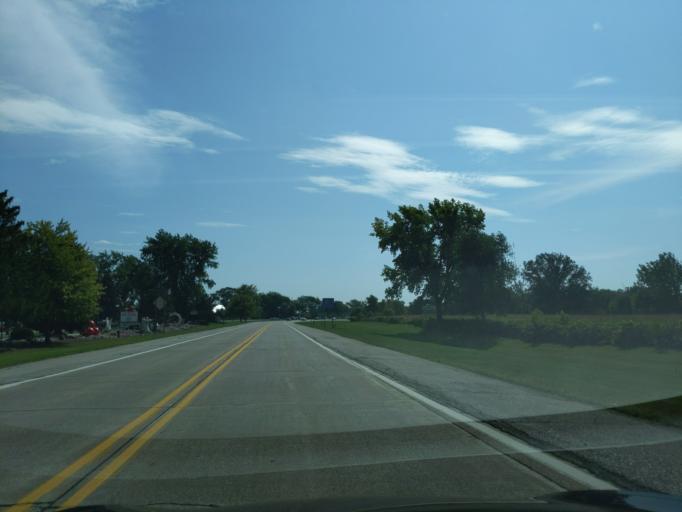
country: US
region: Michigan
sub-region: Saginaw County
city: Frankenmuth
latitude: 43.3131
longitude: -83.7379
